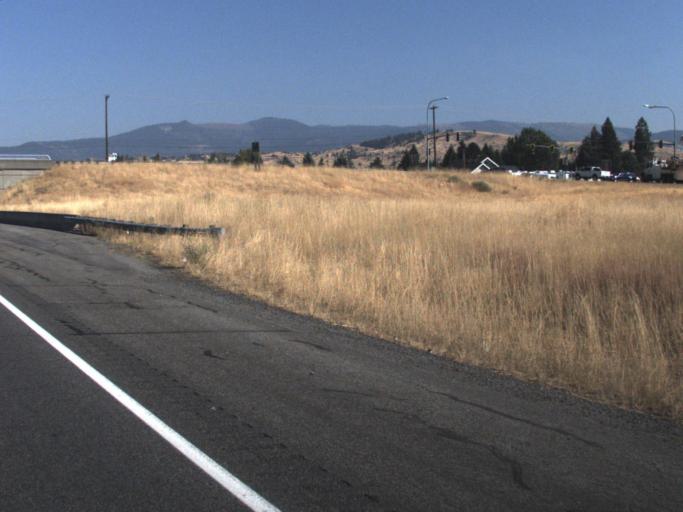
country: US
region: Washington
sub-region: Spokane County
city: Liberty Lake
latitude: 47.6655
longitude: -117.1552
